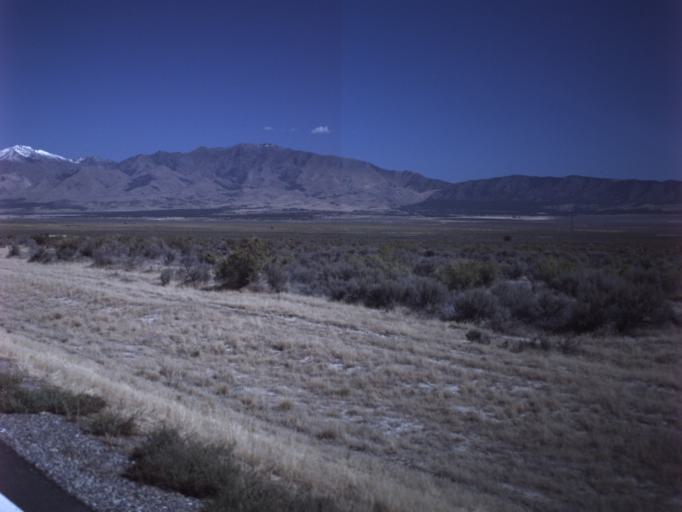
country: US
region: Utah
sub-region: Tooele County
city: Grantsville
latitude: 40.2416
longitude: -112.7232
